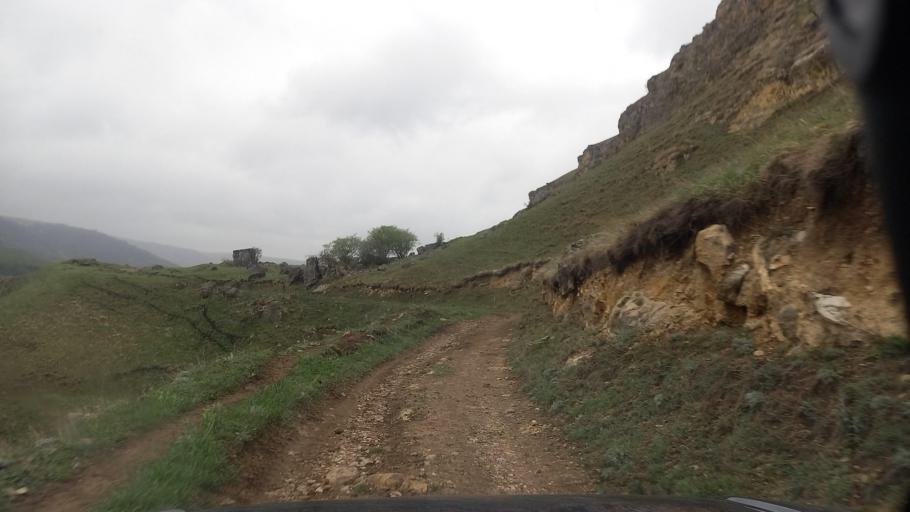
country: RU
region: Stavropol'skiy
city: Nezhinskiy
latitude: 43.8504
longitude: 42.6371
